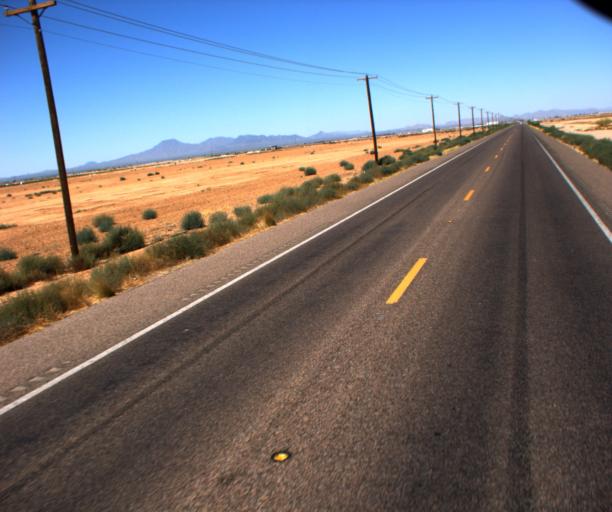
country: US
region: Arizona
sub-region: Pinal County
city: Casa Grande
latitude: 32.8795
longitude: -111.8875
